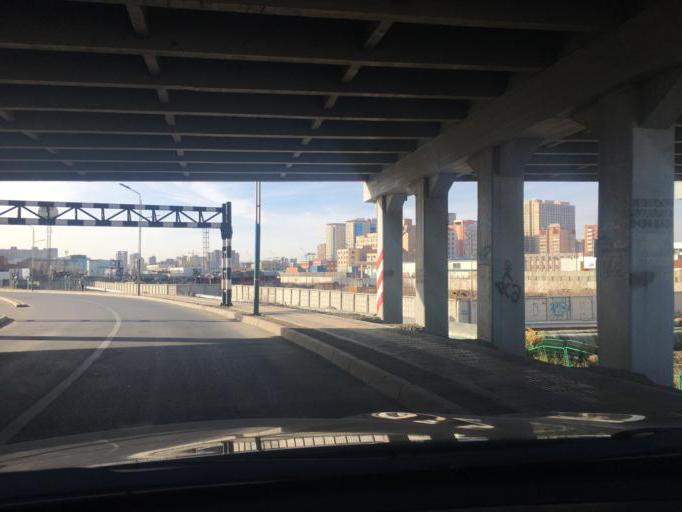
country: MN
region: Ulaanbaatar
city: Ulaanbaatar
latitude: 47.9070
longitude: 106.9129
